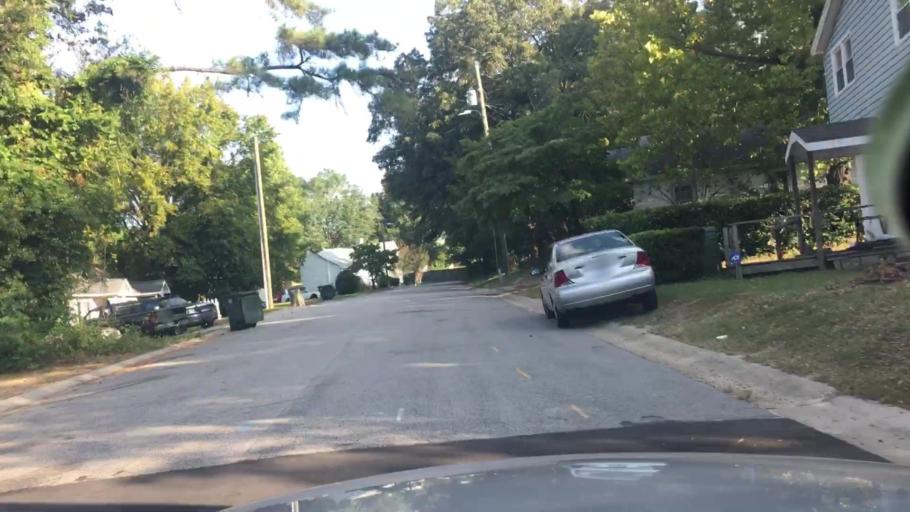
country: US
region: North Carolina
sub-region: Cumberland County
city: Fayetteville
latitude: 35.0490
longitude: -78.8924
